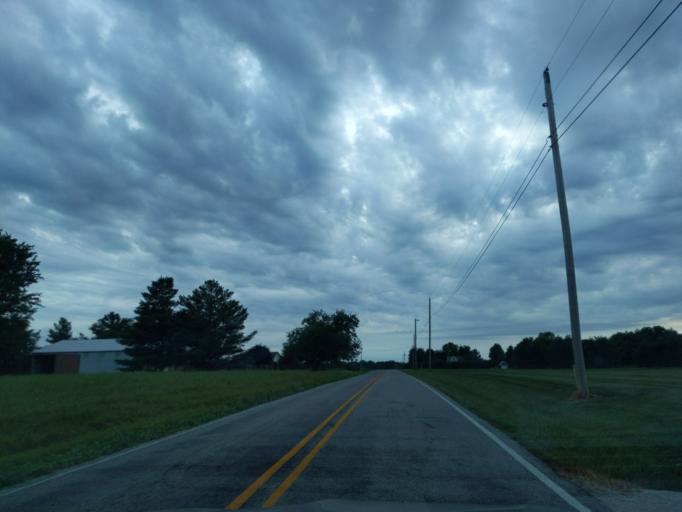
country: US
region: Indiana
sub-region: Ripley County
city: Sunman
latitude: 39.2031
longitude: -85.1679
